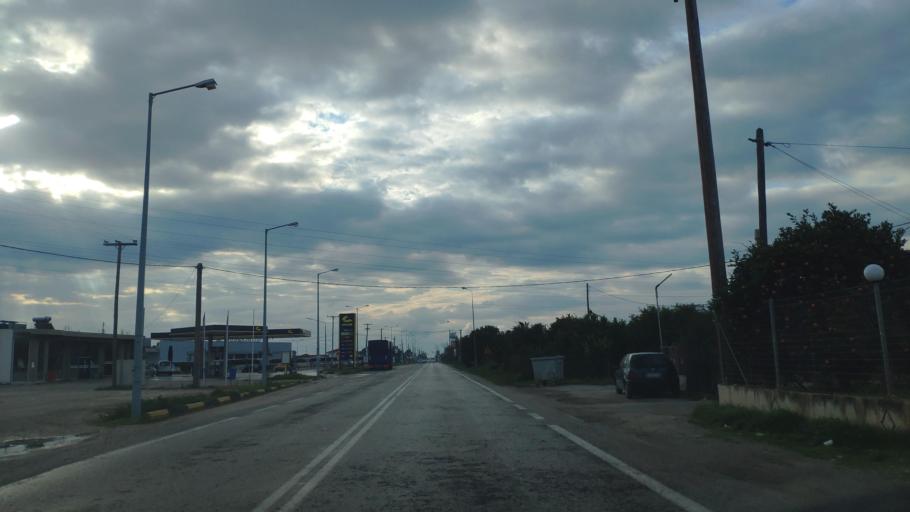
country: GR
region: Peloponnese
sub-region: Nomos Argolidos
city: Argos
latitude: 37.6579
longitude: 22.7263
